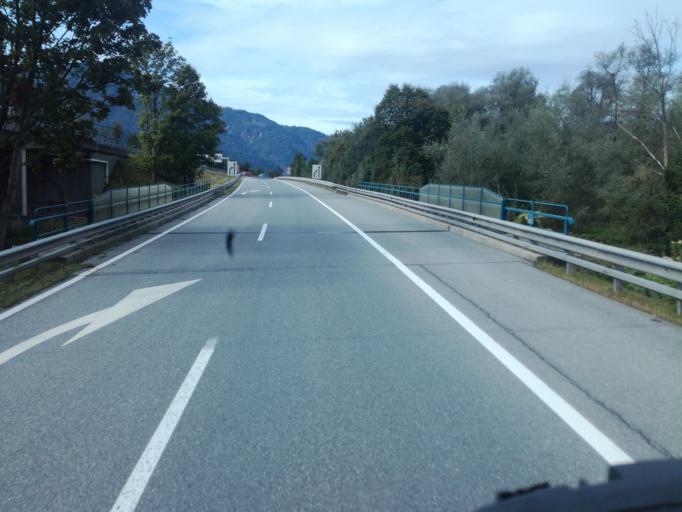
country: AT
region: Tyrol
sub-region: Politischer Bezirk Kufstein
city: Angath
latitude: 47.4927
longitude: 12.0559
